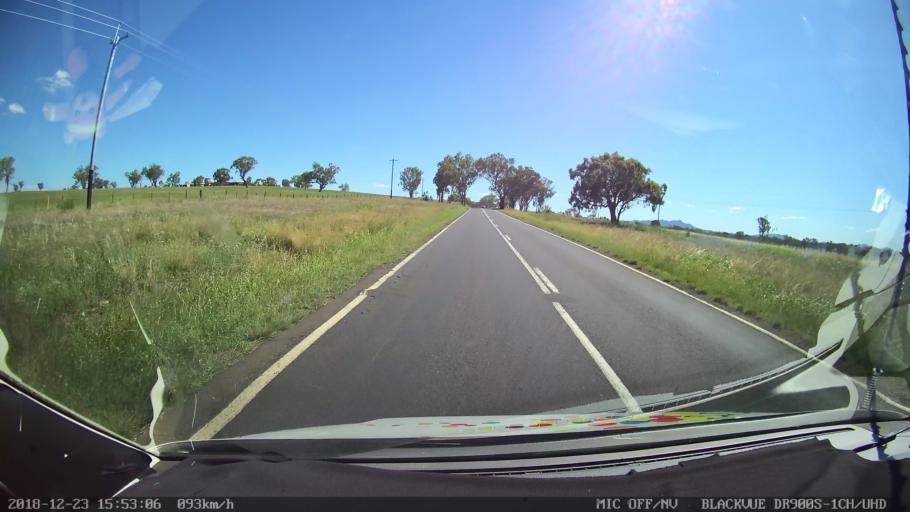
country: AU
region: New South Wales
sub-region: Tamworth Municipality
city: Phillip
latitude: -31.1292
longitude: 150.8835
